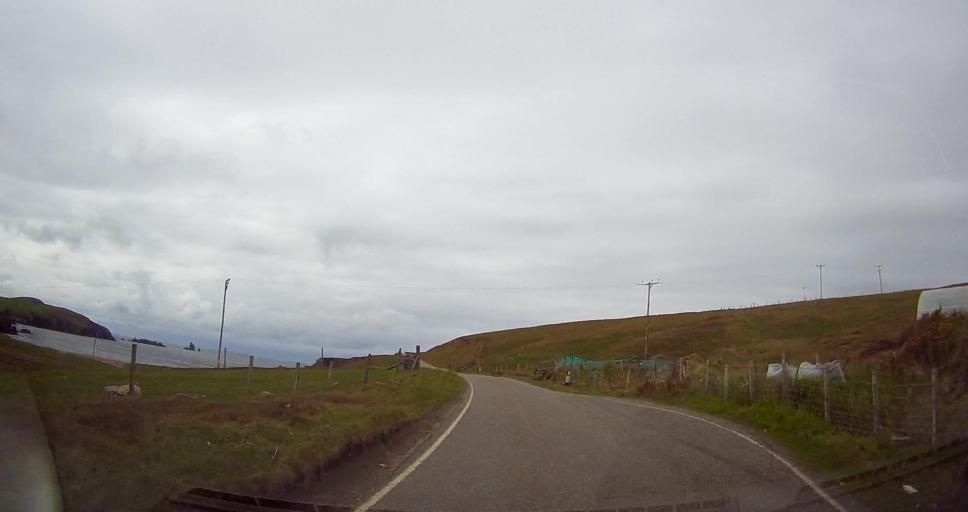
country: GB
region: Scotland
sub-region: Shetland Islands
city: Lerwick
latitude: 60.4884
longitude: -1.4939
